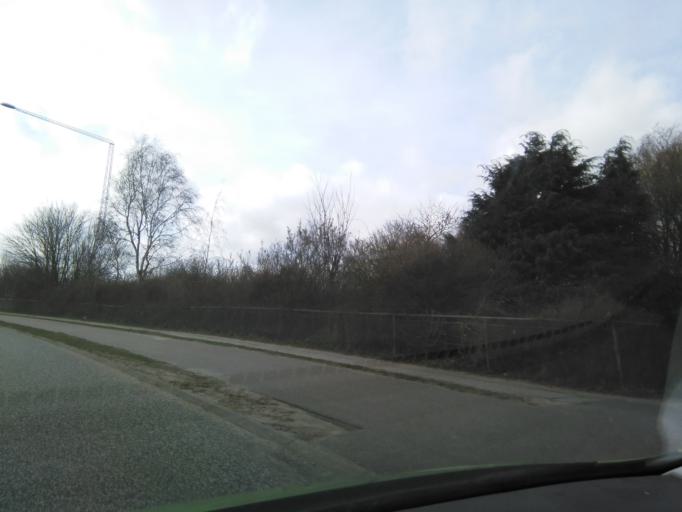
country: DK
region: Central Jutland
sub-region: Arhus Kommune
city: Arhus
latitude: 56.2008
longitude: 10.1955
